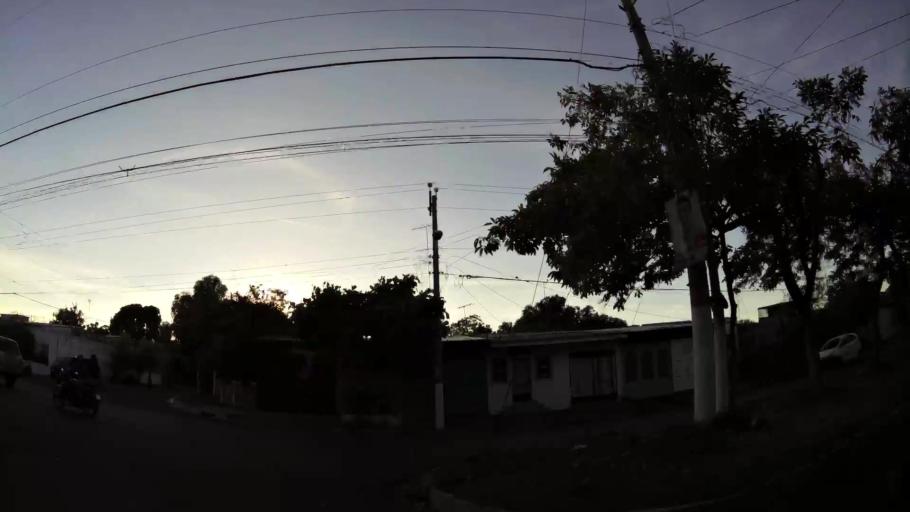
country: SV
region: San Miguel
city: San Miguel
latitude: 13.4761
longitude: -88.1638
